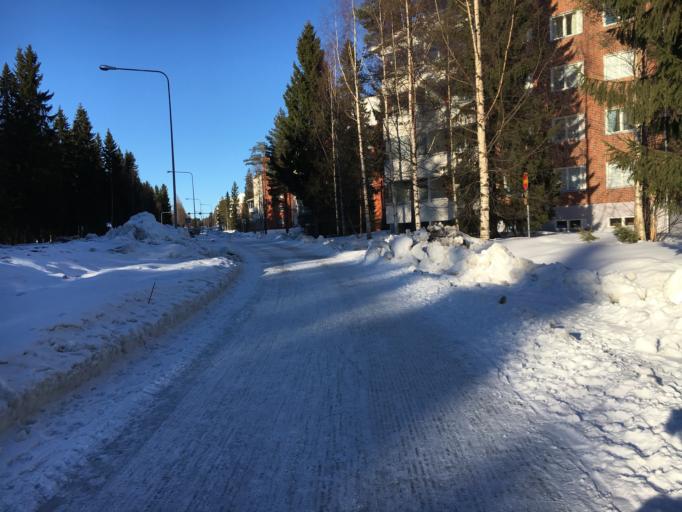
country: FI
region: Kainuu
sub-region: Kajaani
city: Kajaani
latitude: 64.2280
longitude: 27.7518
